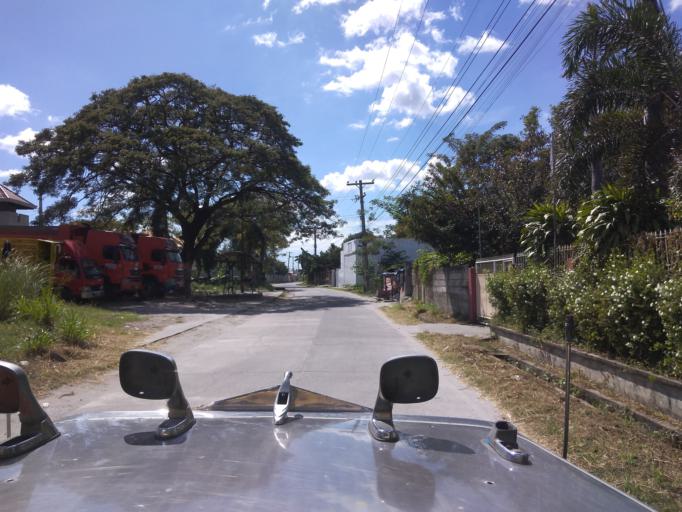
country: PH
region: Central Luzon
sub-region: Province of Pampanga
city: Magliman
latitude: 15.0372
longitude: 120.6531
